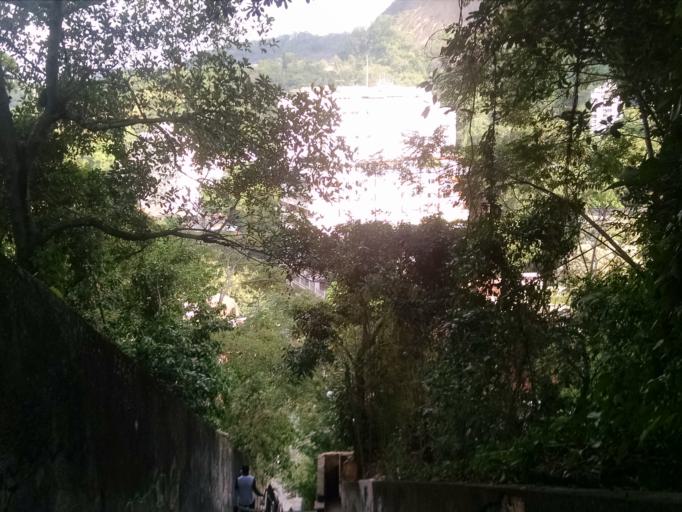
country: BR
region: Rio de Janeiro
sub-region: Rio De Janeiro
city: Rio de Janeiro
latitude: -22.9372
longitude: -43.1987
